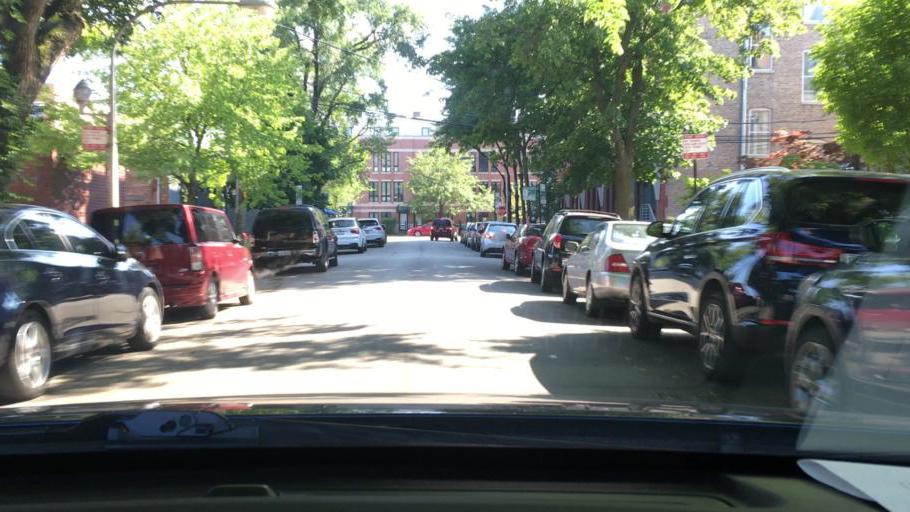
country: US
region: Illinois
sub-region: Cook County
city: Chicago
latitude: 41.9406
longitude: -87.6614
